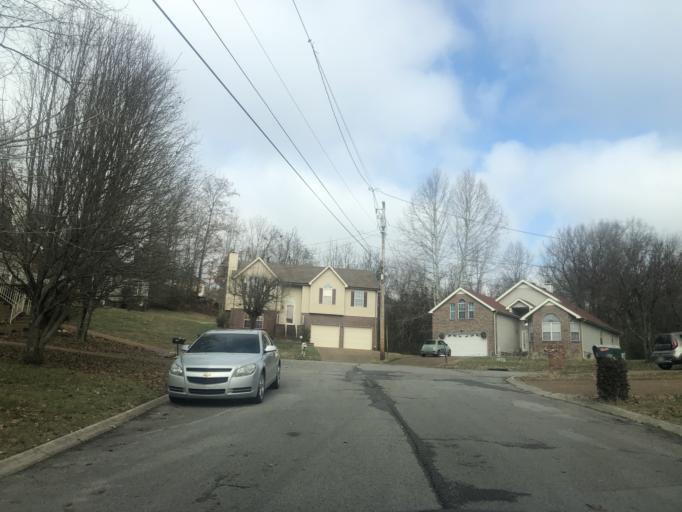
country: US
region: Tennessee
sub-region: Rutherford County
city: La Vergne
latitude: 36.0747
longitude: -86.6519
